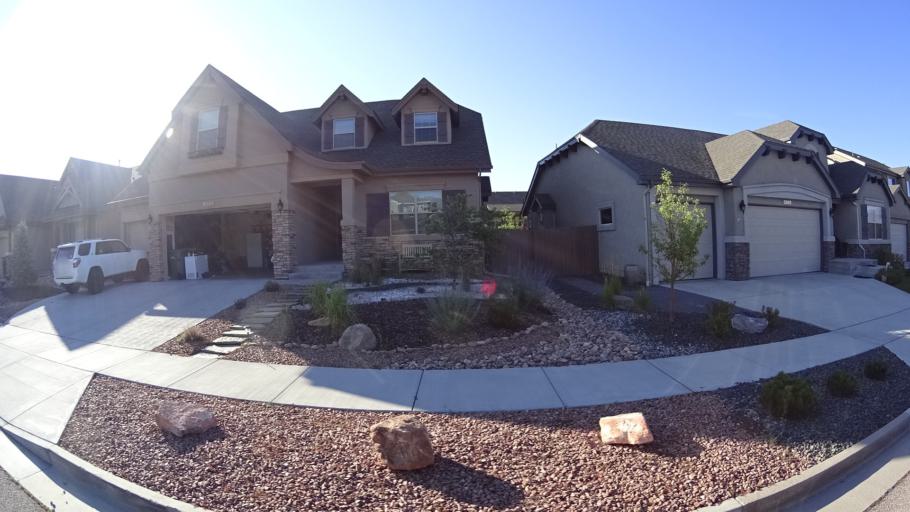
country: US
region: Colorado
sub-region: El Paso County
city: Black Forest
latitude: 38.9839
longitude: -104.7715
